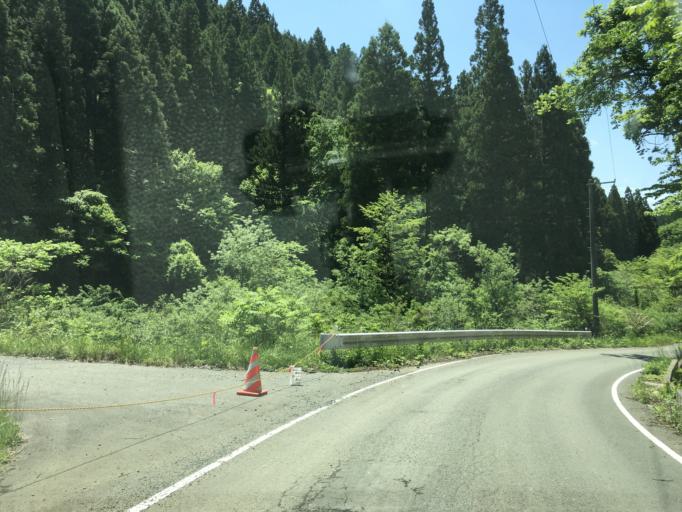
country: JP
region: Miyagi
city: Wakuya
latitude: 38.6866
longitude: 141.3477
